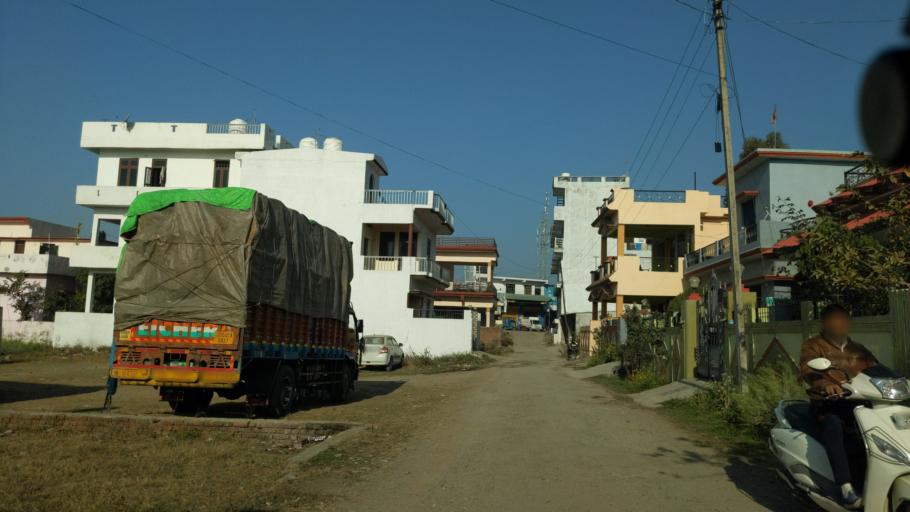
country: IN
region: Uttarakhand
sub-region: Naini Tal
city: Haldwani
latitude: 29.2075
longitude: 79.4955
